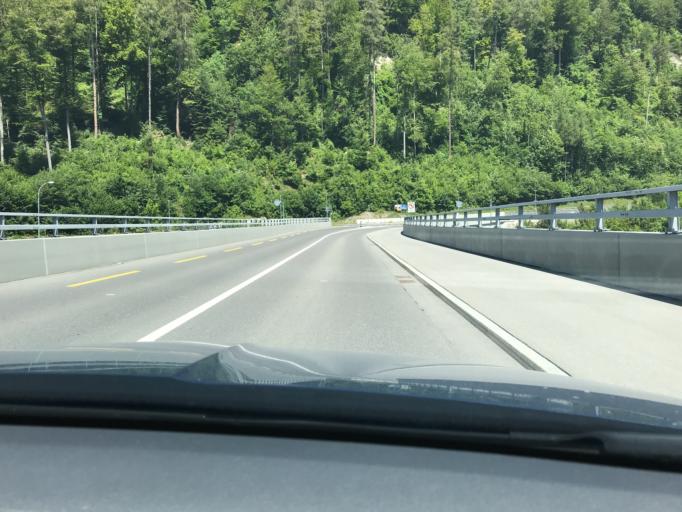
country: CH
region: Bern
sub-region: Interlaken-Oberhasli District
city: Interlaken
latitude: 46.6935
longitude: 7.8715
